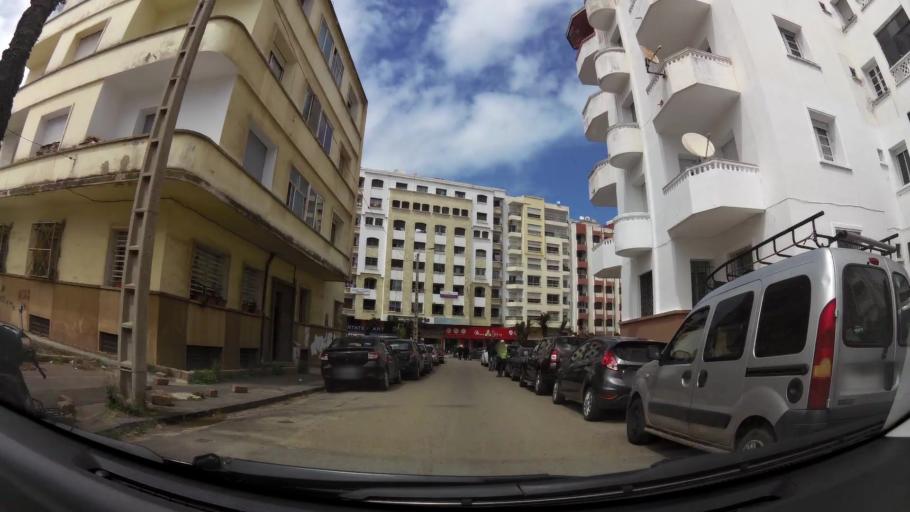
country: MA
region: Grand Casablanca
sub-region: Casablanca
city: Casablanca
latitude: 33.5950
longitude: -7.6389
